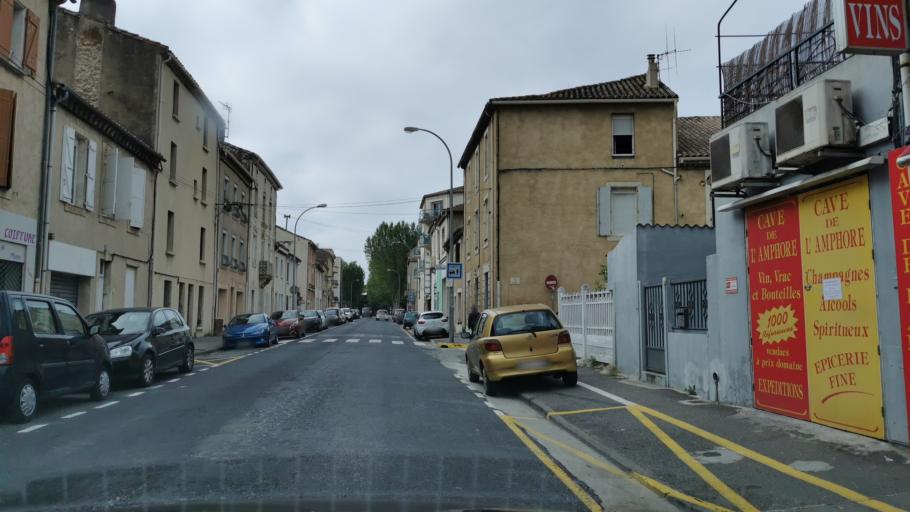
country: FR
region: Languedoc-Roussillon
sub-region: Departement de l'Aude
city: Narbonne
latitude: 43.1901
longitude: 3.0091
